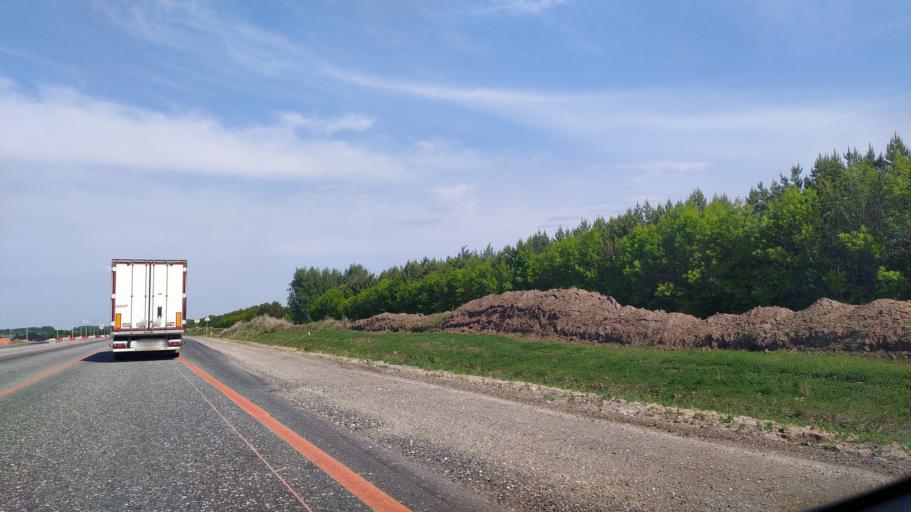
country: RU
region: Mariy-El
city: Volzhsk
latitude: 55.7266
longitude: 48.3734
